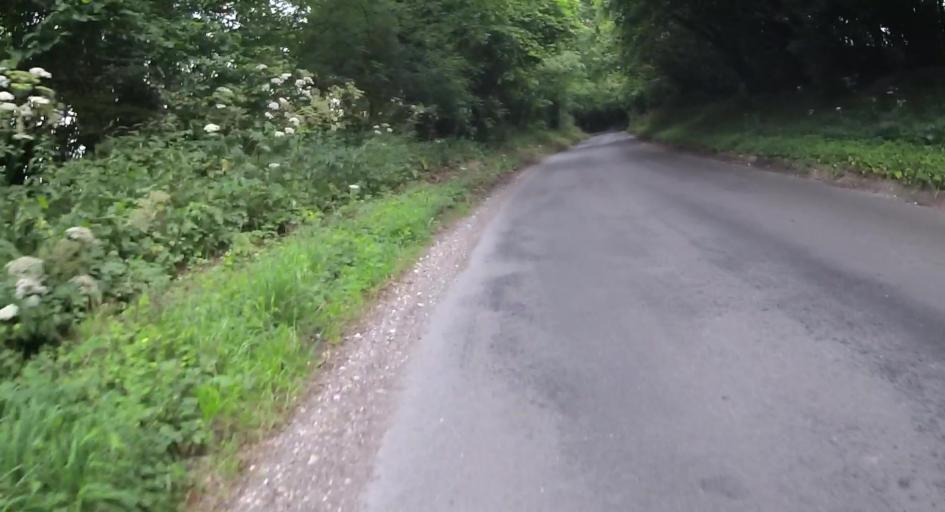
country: GB
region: England
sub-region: Hampshire
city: Bishops Waltham
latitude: 51.0245
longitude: -1.2026
